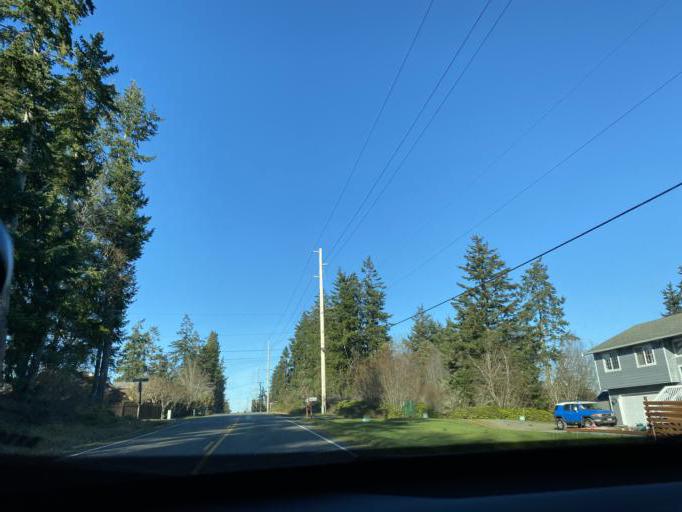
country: US
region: Washington
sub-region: Island County
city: Camano
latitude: 48.1230
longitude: -122.5633
